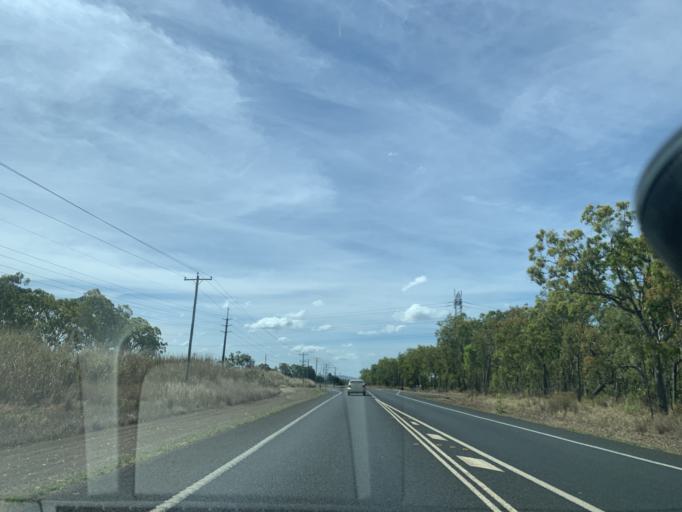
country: AU
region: Queensland
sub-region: Tablelands
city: Tolga
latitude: -17.1387
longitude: 145.4314
